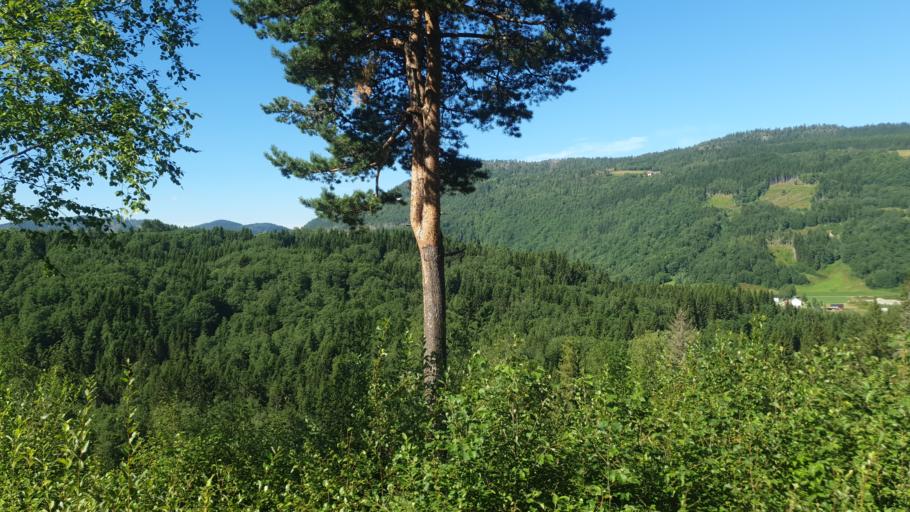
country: NO
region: Sor-Trondelag
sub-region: Meldal
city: Meldal
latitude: 63.1565
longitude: 9.7257
